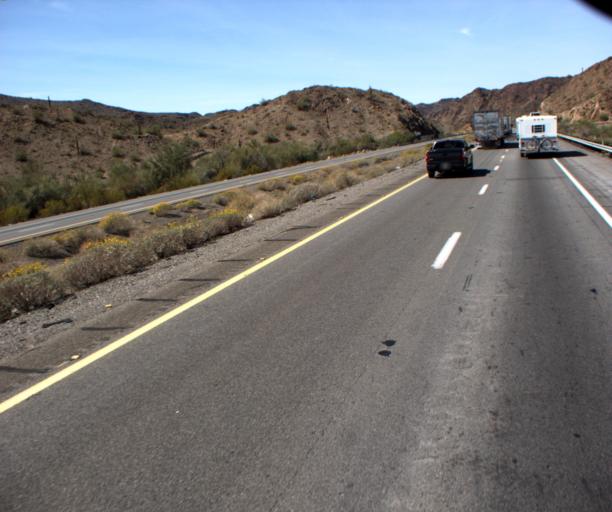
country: US
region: Arizona
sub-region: La Paz County
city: Quartzsite
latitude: 33.6486
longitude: -114.3614
